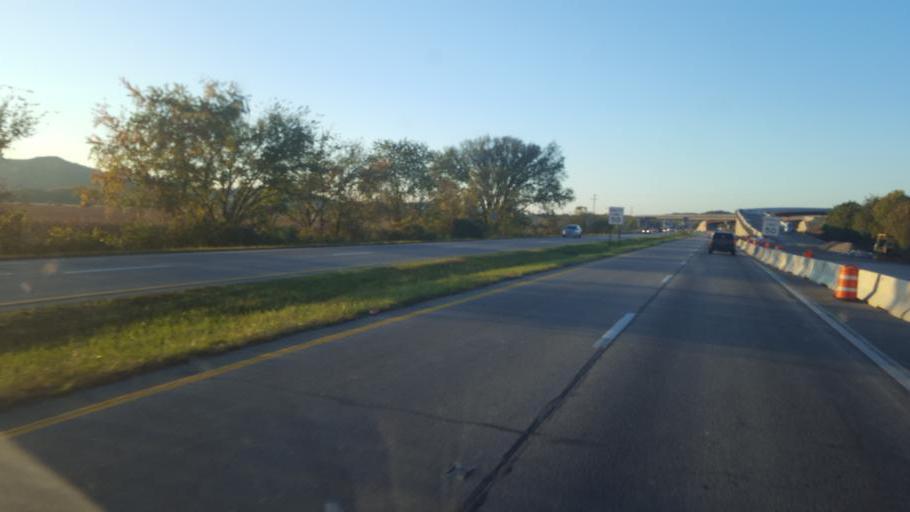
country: US
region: Ohio
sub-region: Scioto County
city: Lucasville
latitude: 38.8874
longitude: -82.9978
